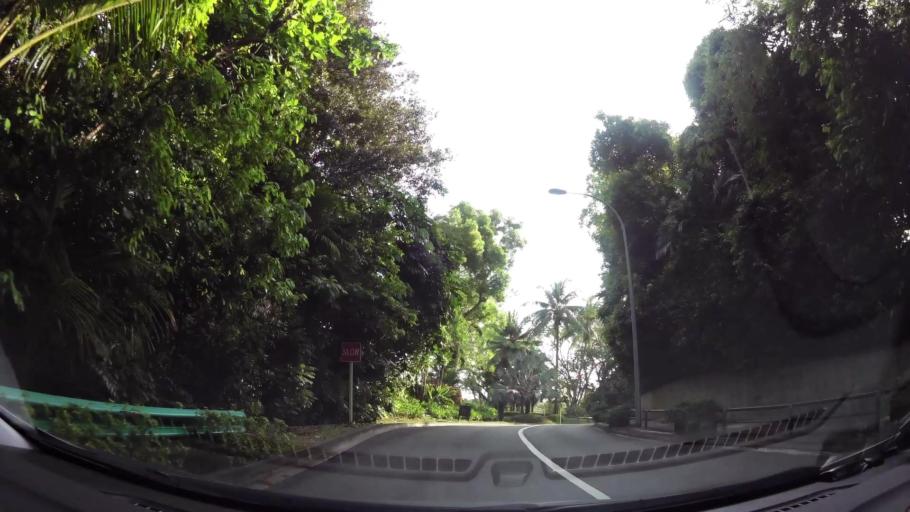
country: SG
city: Singapore
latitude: 1.2482
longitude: 103.8262
